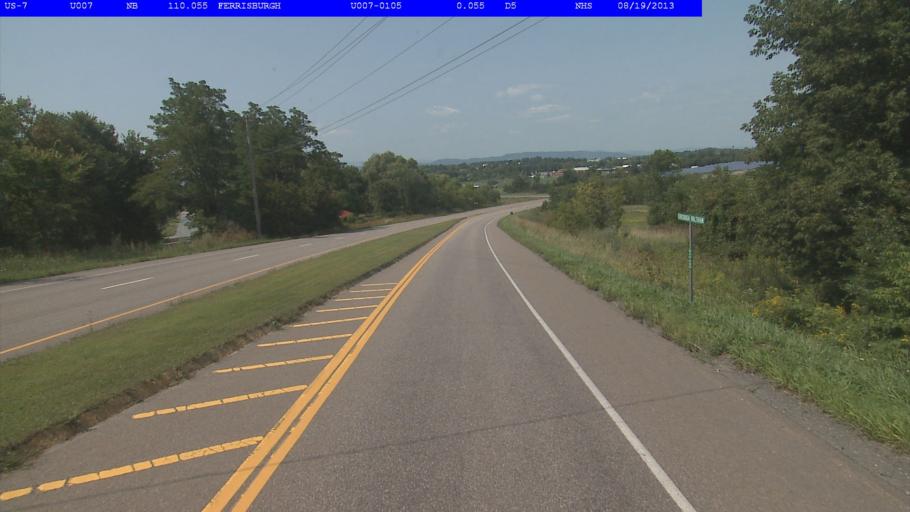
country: US
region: Vermont
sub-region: Addison County
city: Vergennes
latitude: 44.1635
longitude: -73.2357
